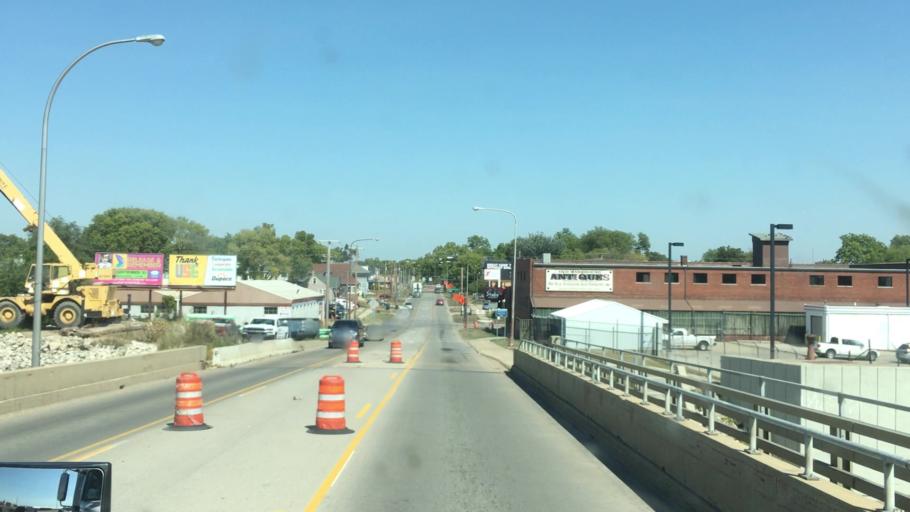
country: US
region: Iowa
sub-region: Black Hawk County
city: Waterloo
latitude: 42.5001
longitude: -92.3413
